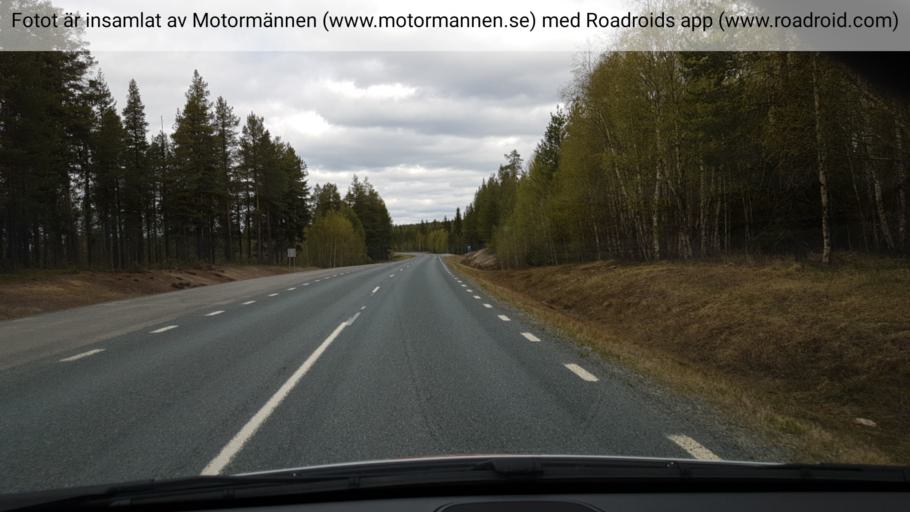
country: SE
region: Vaesterbotten
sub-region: Lycksele Kommun
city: Soderfors
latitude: 65.1785
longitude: 18.2419
